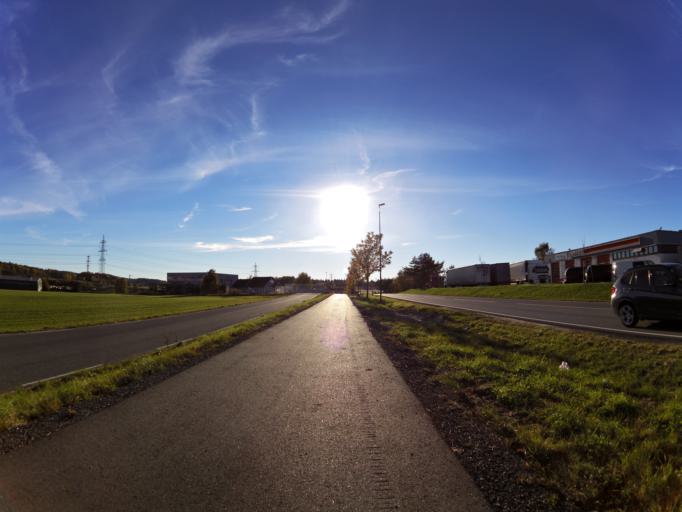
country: NO
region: Ostfold
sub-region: Sarpsborg
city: Sarpsborg
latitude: 59.2633
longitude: 11.1172
